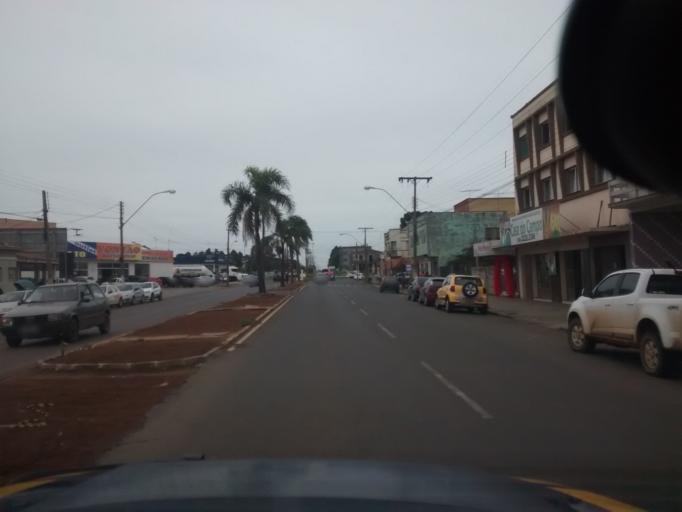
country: BR
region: Rio Grande do Sul
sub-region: Vacaria
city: Vacaria
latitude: -28.5126
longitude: -50.9352
